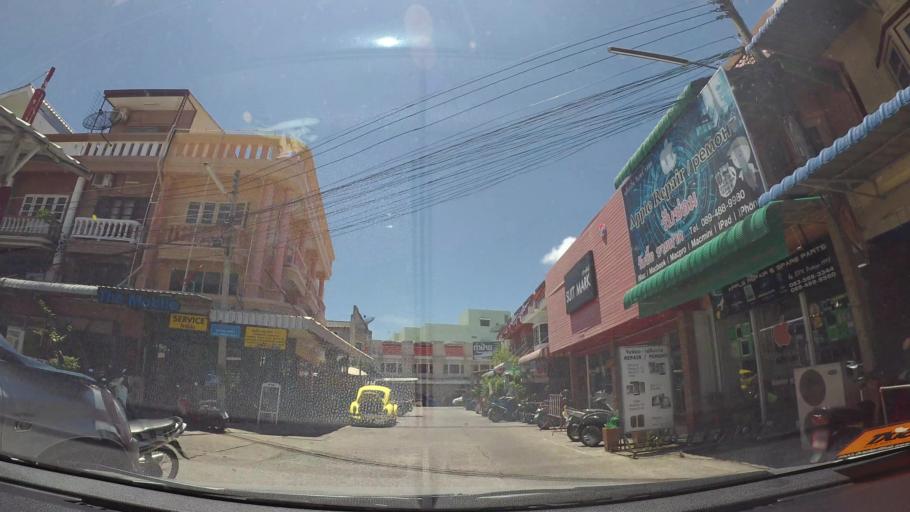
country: TH
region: Chon Buri
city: Phatthaya
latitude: 12.9227
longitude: 100.8794
